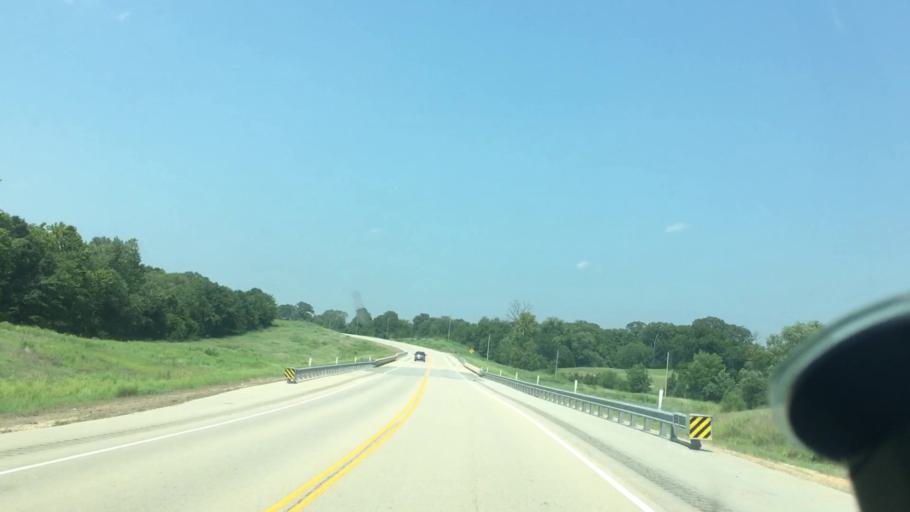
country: US
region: Oklahoma
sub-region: Atoka County
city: Atoka
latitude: 34.2856
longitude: -95.9573
